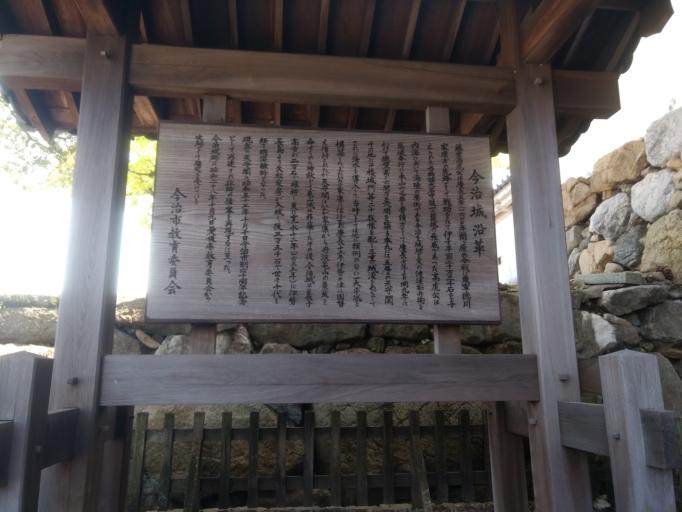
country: JP
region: Ehime
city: Saijo
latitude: 34.0634
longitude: 133.0070
